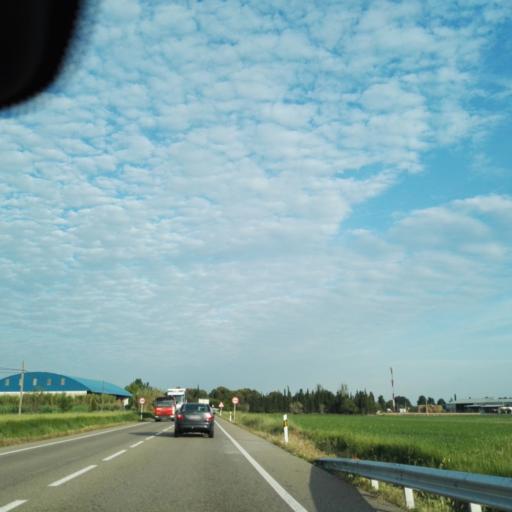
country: ES
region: Aragon
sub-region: Provincia de Zaragoza
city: Oliver-Valdefierro, Oliver, Valdefierro
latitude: 41.6632
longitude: -0.9640
